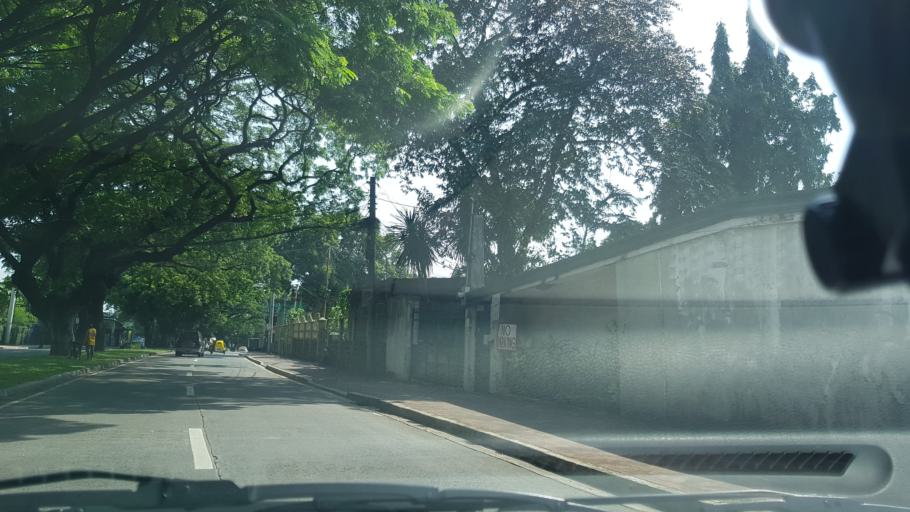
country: PH
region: Calabarzon
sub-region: Province of Rizal
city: Antipolo
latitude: 14.6538
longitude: 121.1161
